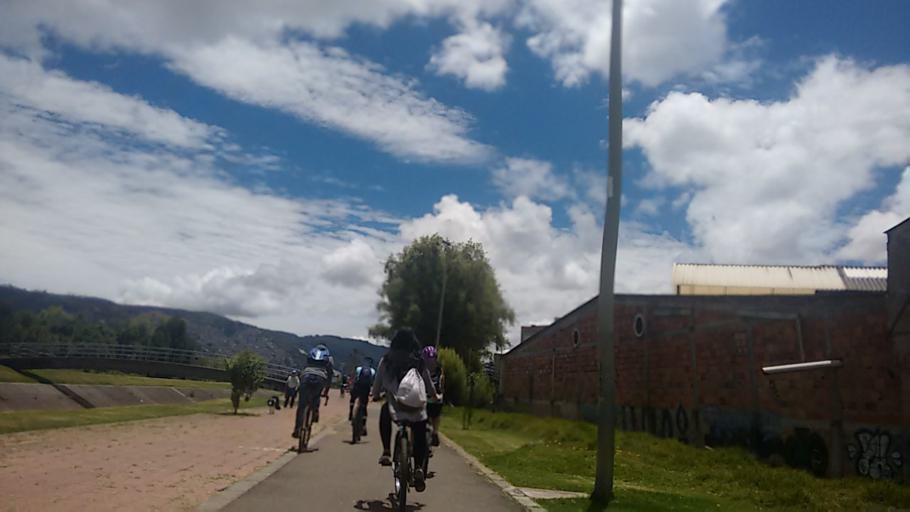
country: CO
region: Cundinamarca
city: Cota
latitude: 4.7757
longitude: -74.0402
